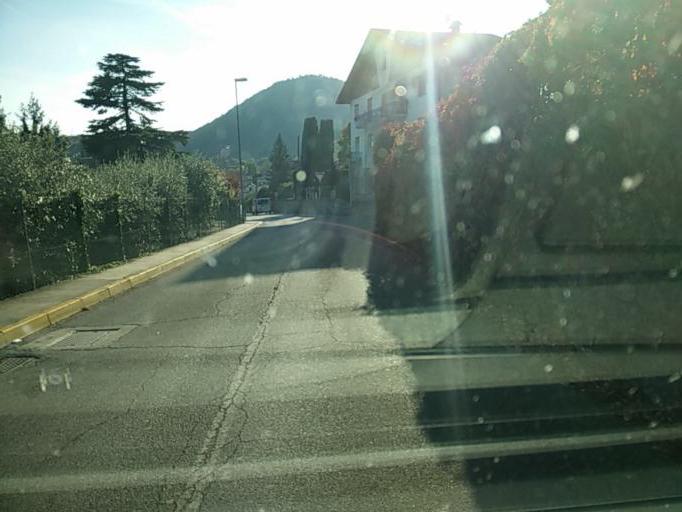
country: IT
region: Lombardy
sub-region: Provincia di Brescia
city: Roe Volciano
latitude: 45.6124
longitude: 10.4835
